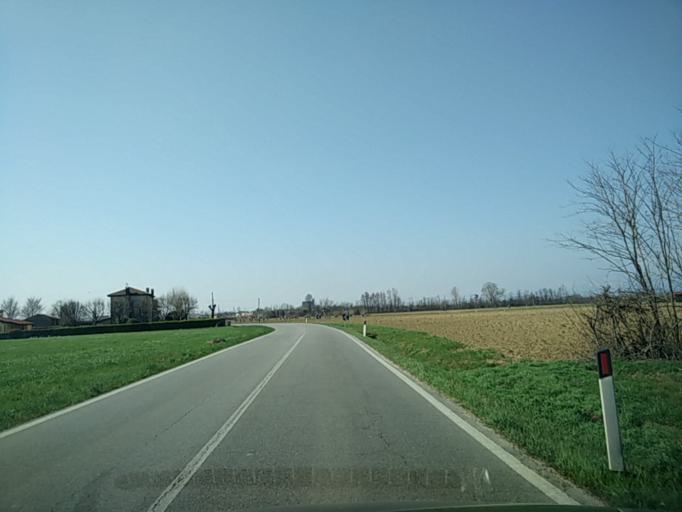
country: IT
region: Veneto
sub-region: Provincia di Treviso
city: Castello di Godego
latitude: 45.6998
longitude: 11.8996
